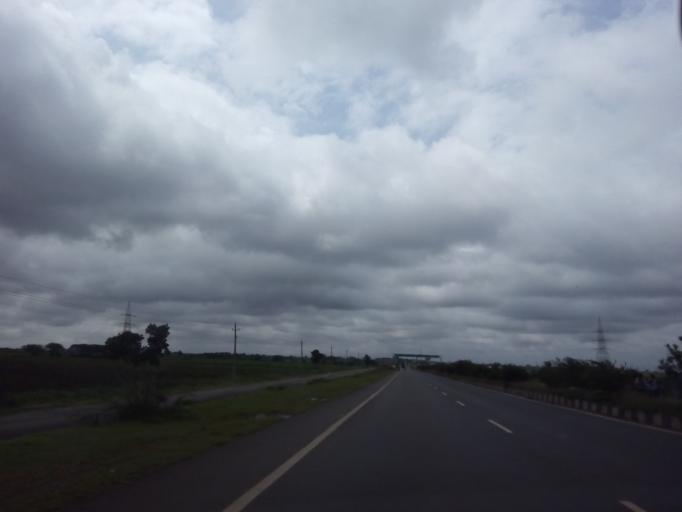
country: IN
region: Karnataka
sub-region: Haveri
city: Haveri
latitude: 14.8360
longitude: 75.3565
